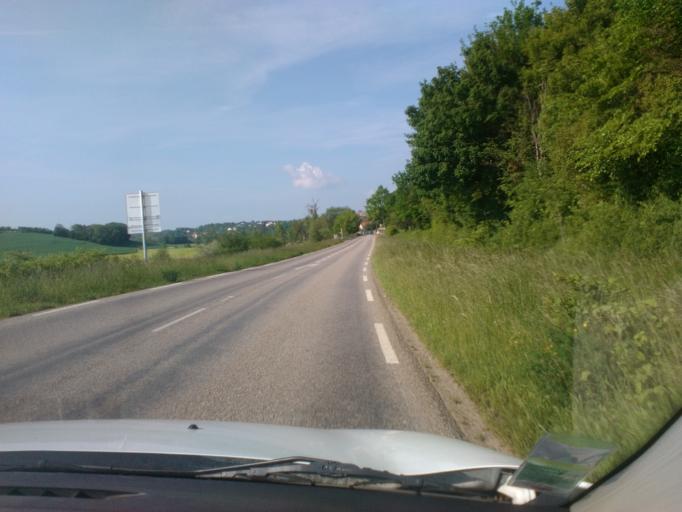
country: FR
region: Lorraine
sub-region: Departement des Vosges
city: Mirecourt
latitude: 48.3285
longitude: 6.1329
